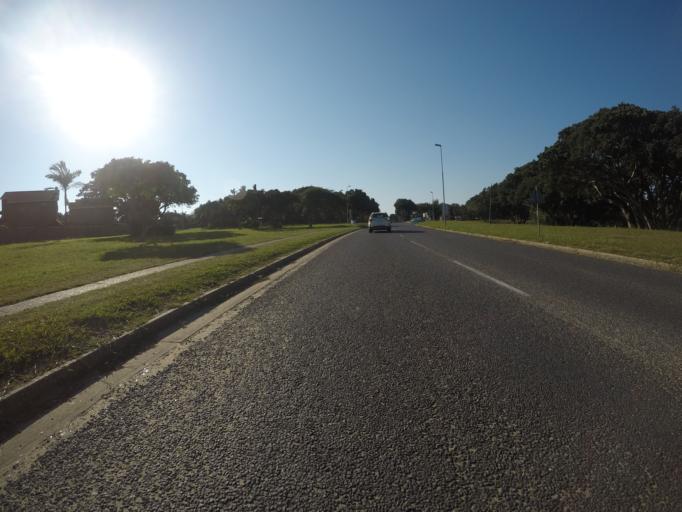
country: ZA
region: KwaZulu-Natal
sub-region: uThungulu District Municipality
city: Richards Bay
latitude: -28.7909
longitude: 32.0983
